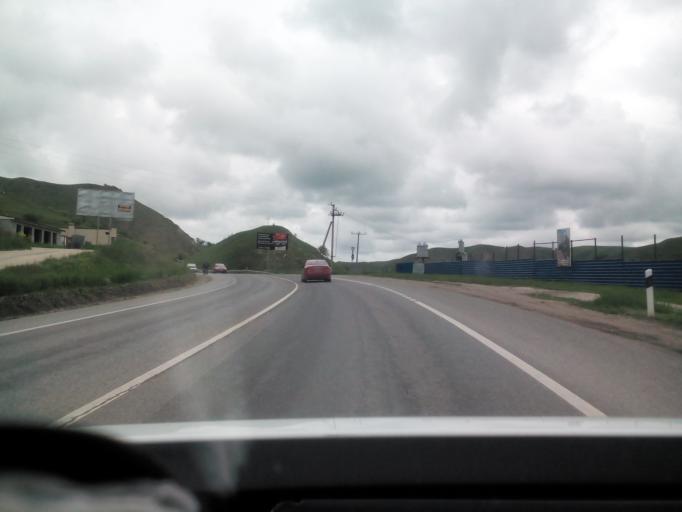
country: RU
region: Stavropol'skiy
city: Yasnaya Polyana
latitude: 43.9732
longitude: 42.7855
